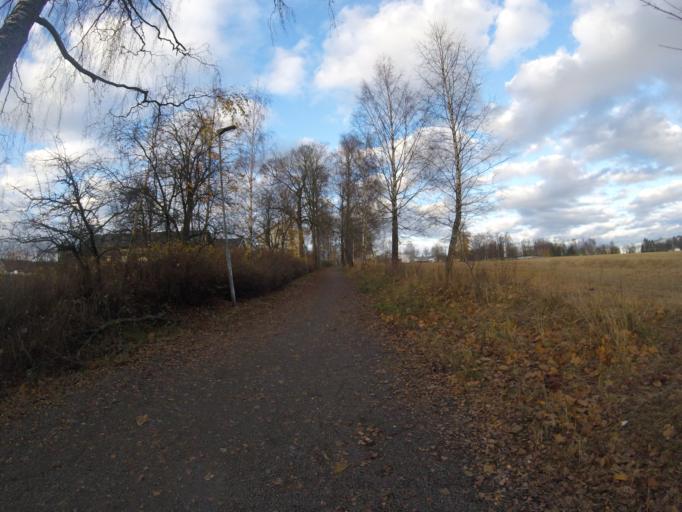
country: NO
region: Akershus
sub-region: Skedsmo
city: Lillestrom
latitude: 59.9921
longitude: 11.0376
